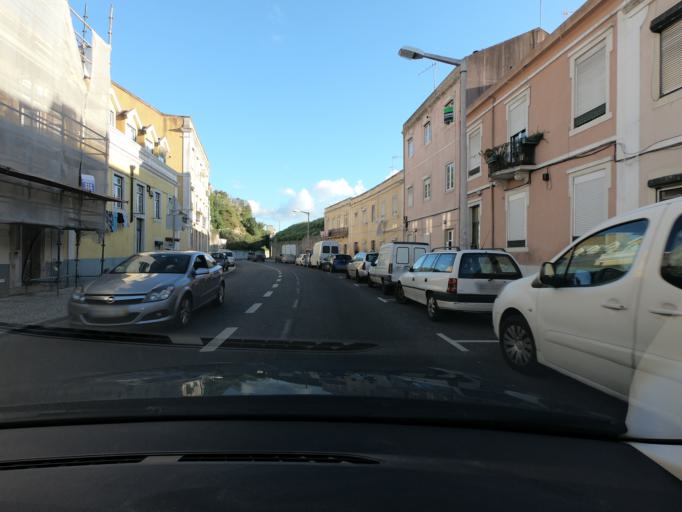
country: PT
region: Lisbon
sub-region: Lisbon
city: Lisbon
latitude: 38.7338
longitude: -9.1173
